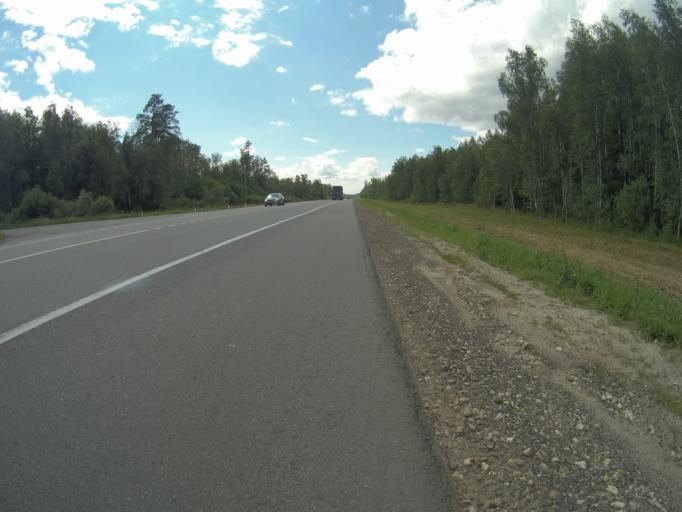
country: RU
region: Vladimir
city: Raduzhnyy
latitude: 56.0720
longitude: 40.2677
